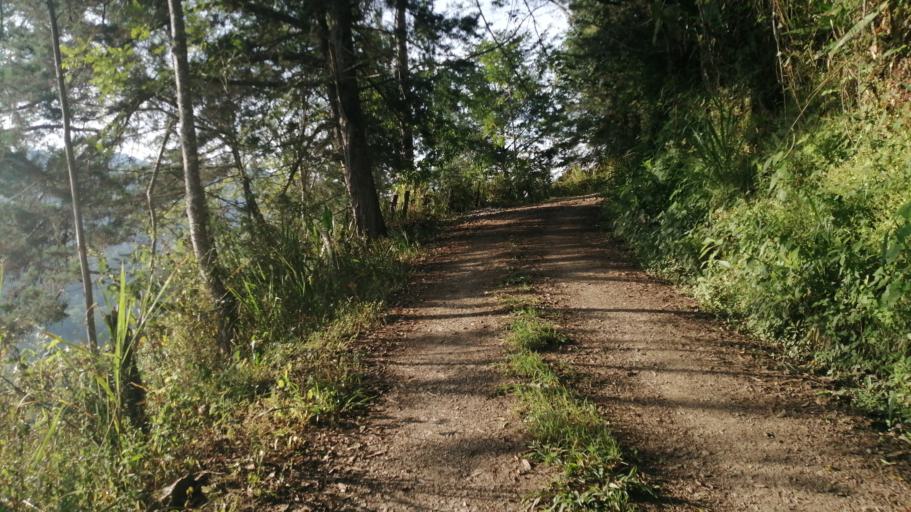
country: CO
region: Boyaca
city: Garagoa
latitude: 5.0789
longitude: -73.3886
